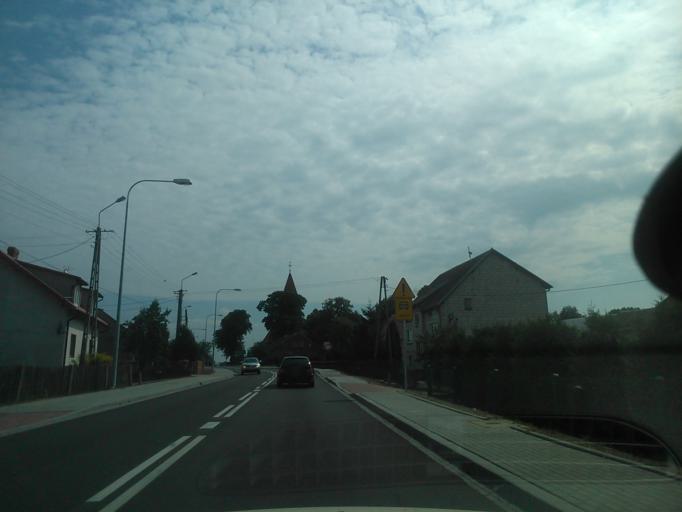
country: PL
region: Warmian-Masurian Voivodeship
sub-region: Powiat dzialdowski
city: Lidzbark
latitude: 53.2351
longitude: 19.9425
